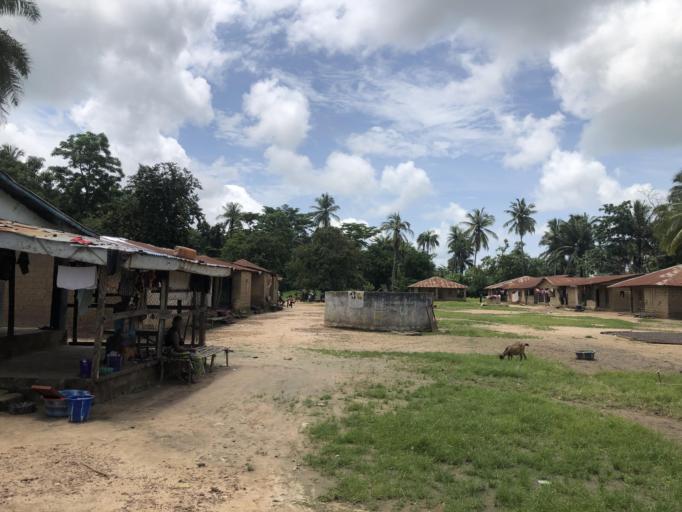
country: SL
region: Northern Province
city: Lunsar
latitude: 8.7606
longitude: -12.4732
